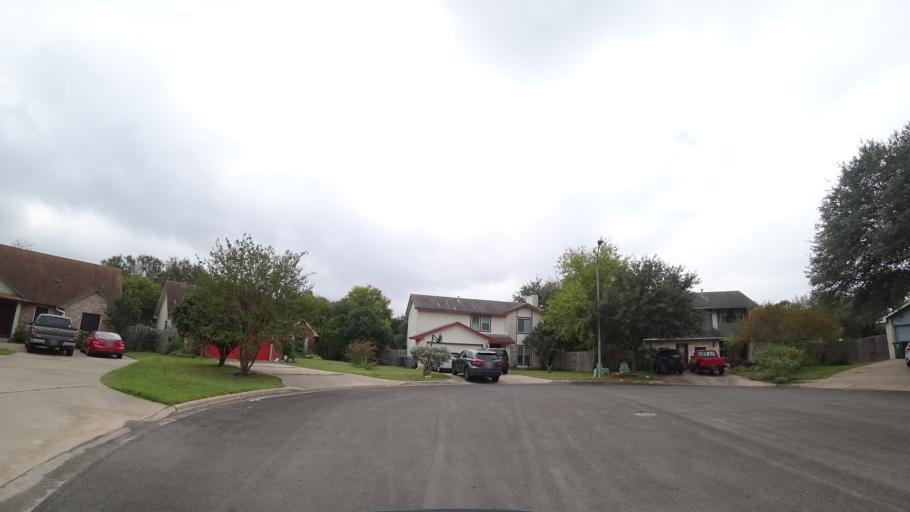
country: US
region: Texas
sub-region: Travis County
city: Shady Hollow
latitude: 30.2065
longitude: -97.8431
